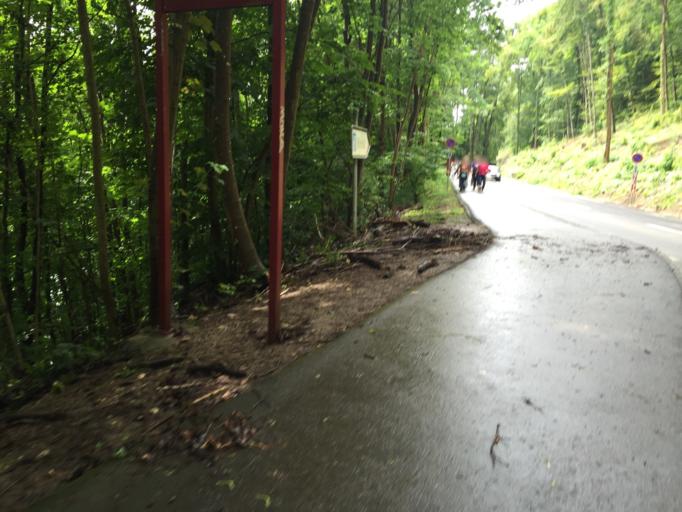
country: CH
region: Schaffhausen
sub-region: Bezirk Schaffhausen
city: Neuhausen
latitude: 47.6759
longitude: 8.6093
